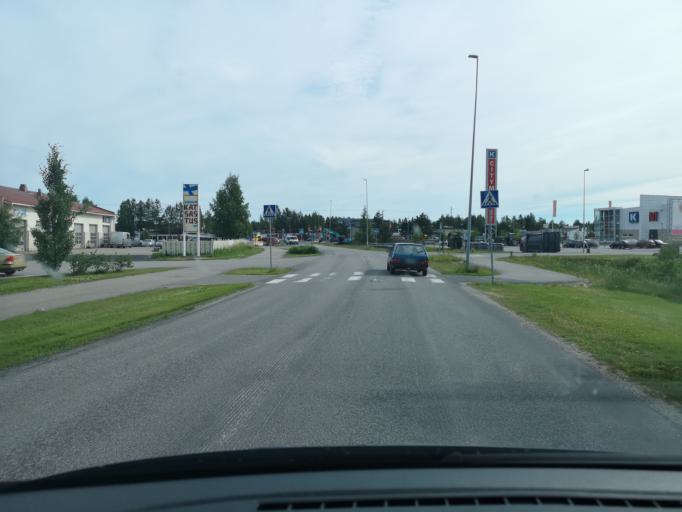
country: FI
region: Northern Ostrobothnia
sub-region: Ylivieska
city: Ylivieska
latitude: 64.0634
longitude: 24.5498
